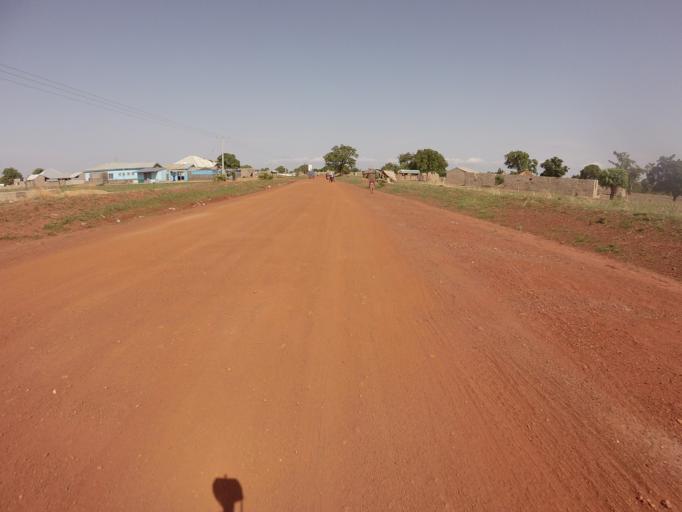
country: GH
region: Upper East
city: Bawku
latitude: 10.8321
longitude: -0.1716
